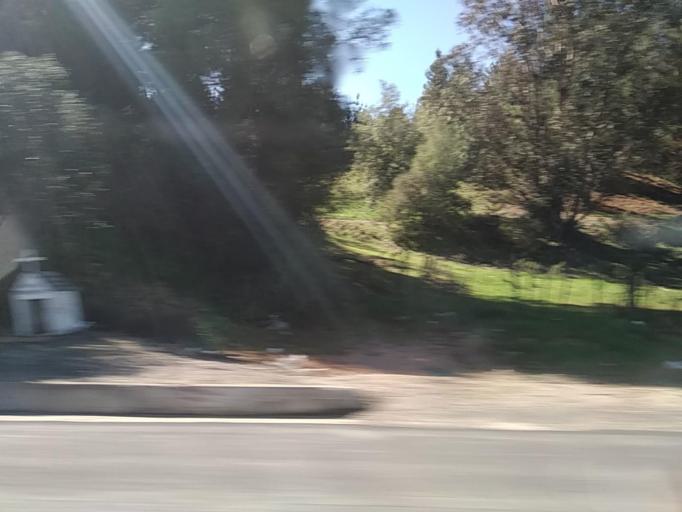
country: CL
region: Valparaiso
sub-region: Provincia de Marga Marga
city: Quilpue
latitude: -33.2256
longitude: -71.4685
